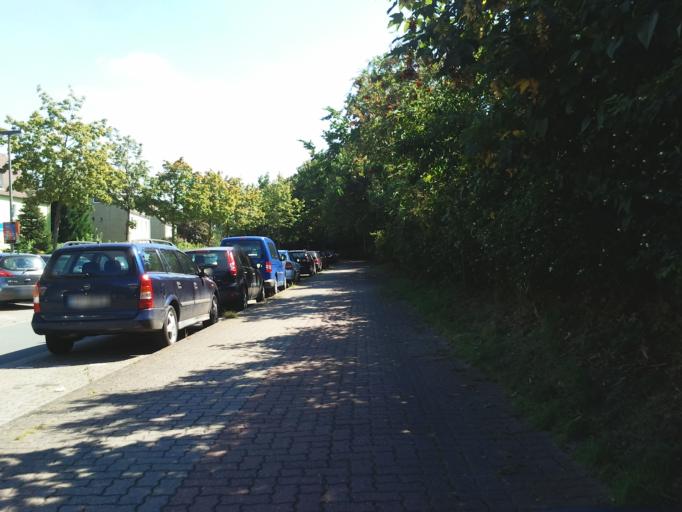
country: DE
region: Lower Saxony
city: Nienburg
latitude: 52.6450
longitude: 9.2189
